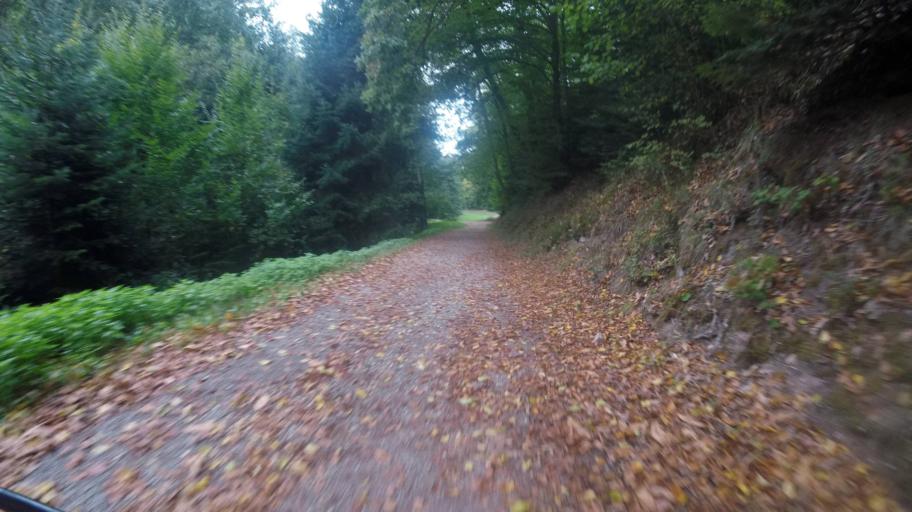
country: DE
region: Baden-Wuerttemberg
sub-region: Karlsruhe Region
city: Gernsbach
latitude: 48.7653
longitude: 8.3624
